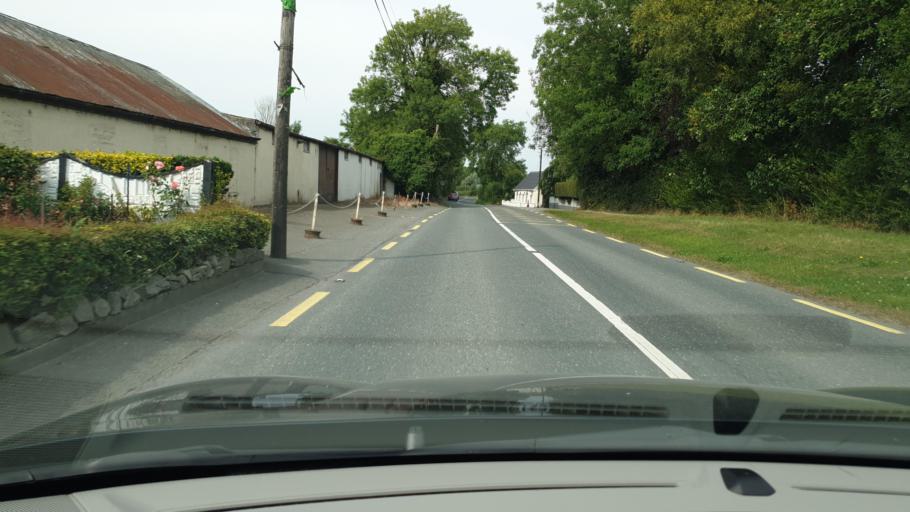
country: IE
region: Leinster
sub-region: An Mhi
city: Newtown Trim
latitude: 53.6292
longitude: -6.7719
